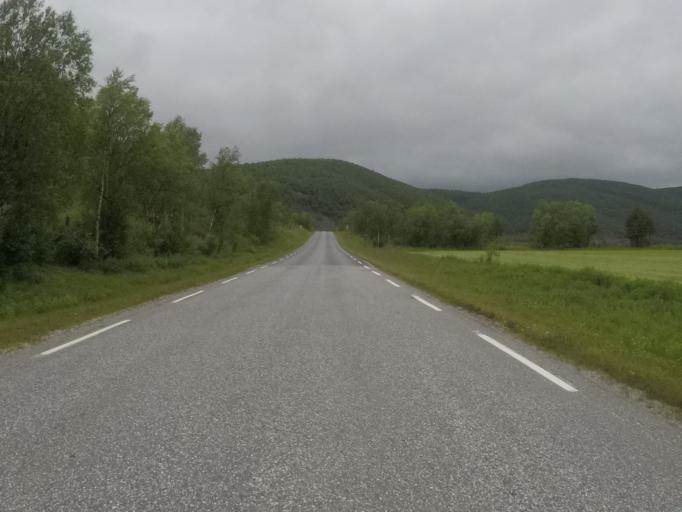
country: NO
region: Finnmark Fylke
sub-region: Karasjok
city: Karasjohka
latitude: 69.6558
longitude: 25.9063
